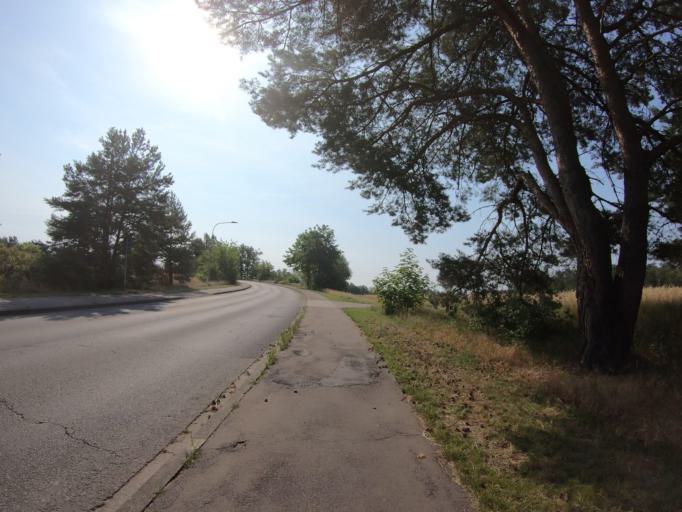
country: DE
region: Lower Saxony
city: Gifhorn
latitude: 52.4918
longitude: 10.5244
